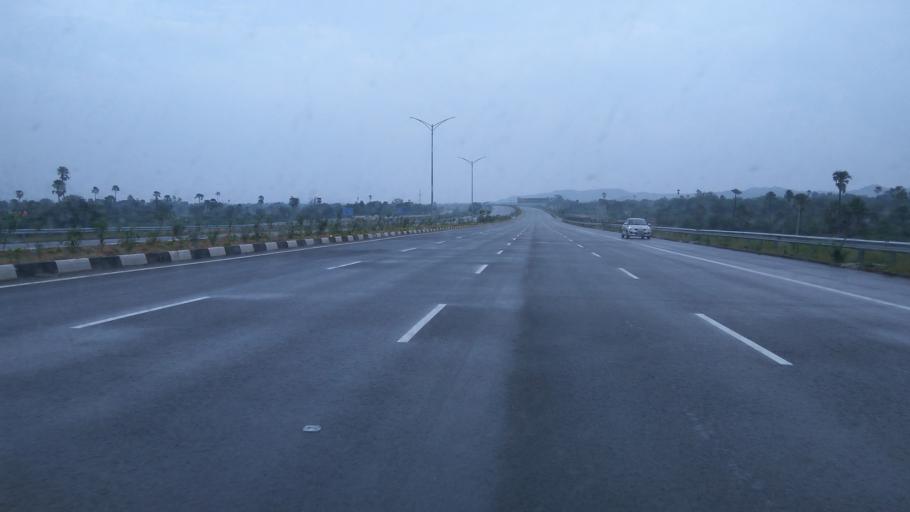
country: IN
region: Telangana
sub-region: Rangareddi
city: Ghatkesar
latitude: 17.4565
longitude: 78.6693
